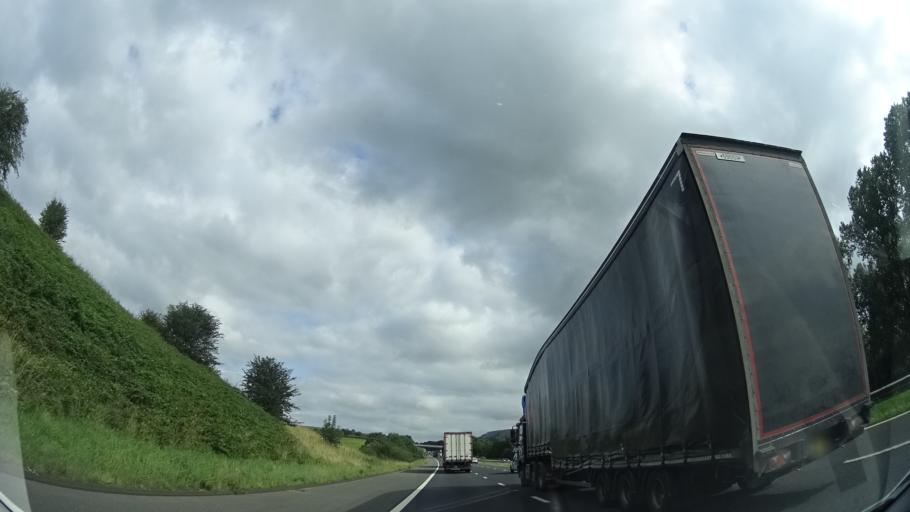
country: GB
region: England
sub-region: Cumbria
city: Milnthorpe
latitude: 54.1890
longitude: -2.7256
